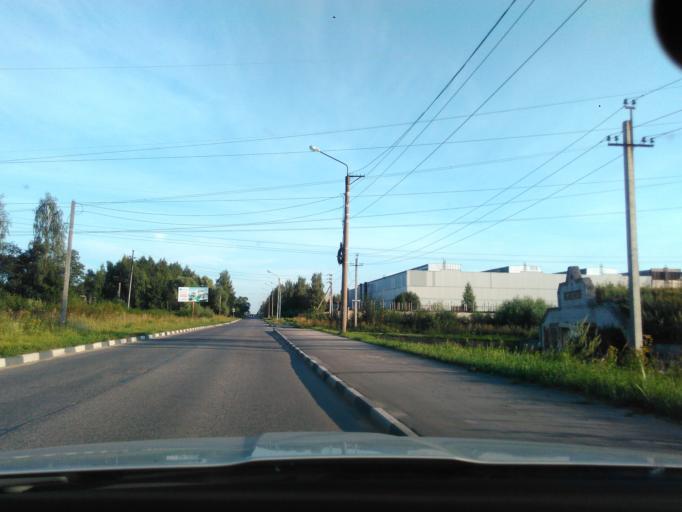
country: RU
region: Tverskaya
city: Konakovo
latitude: 56.7278
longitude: 36.7815
